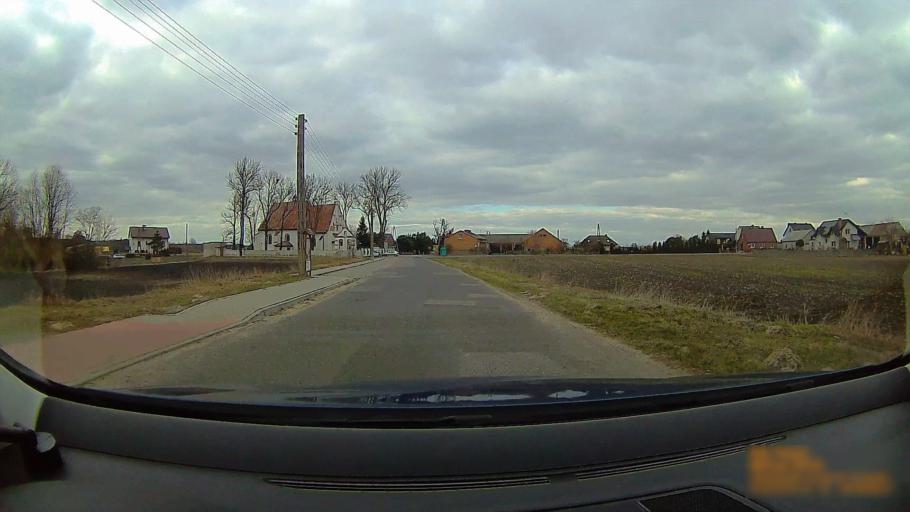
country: PL
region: Greater Poland Voivodeship
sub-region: Powiat koninski
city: Rzgow Pierwszy
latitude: 52.1328
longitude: 18.0581
